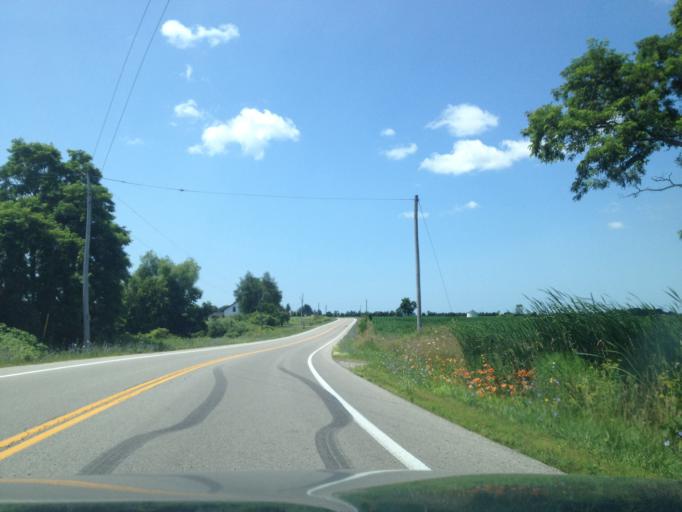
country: CA
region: Ontario
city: Norfolk County
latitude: 42.6071
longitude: -80.4709
